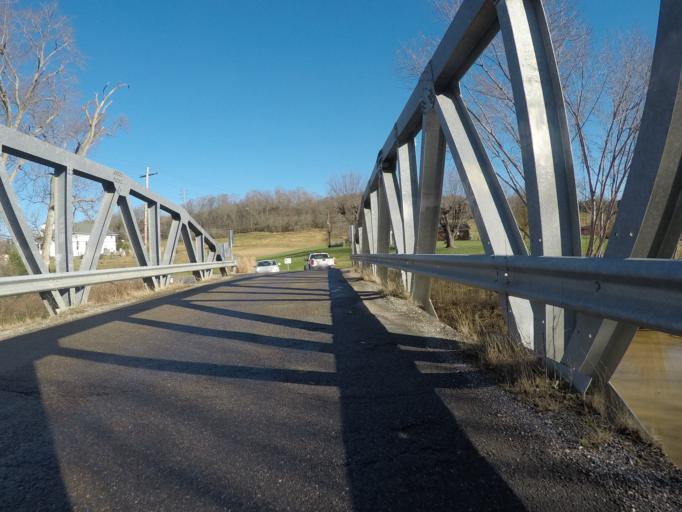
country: US
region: West Virginia
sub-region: Cabell County
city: Huntington
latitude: 38.4860
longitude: -82.4687
